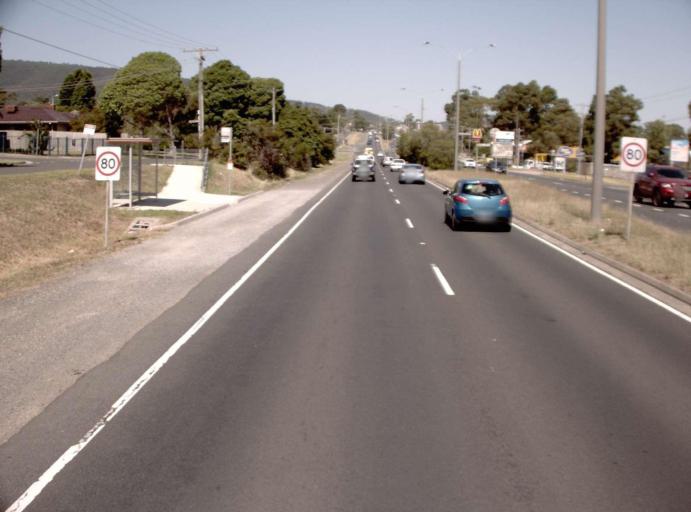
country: AU
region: Victoria
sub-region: Knox
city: Knoxfield
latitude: -37.8785
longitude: 145.2647
